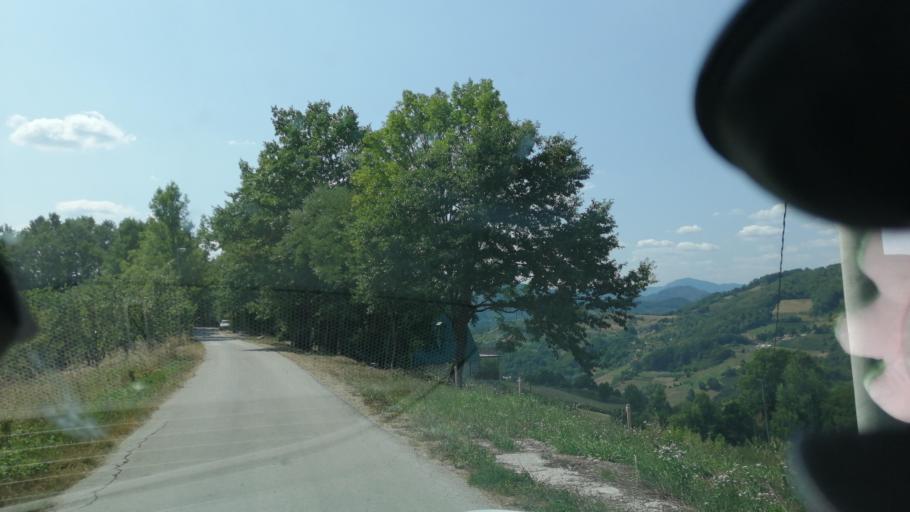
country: RS
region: Central Serbia
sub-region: Moravicki Okrug
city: Ivanjica
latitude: 43.6201
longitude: 20.2493
